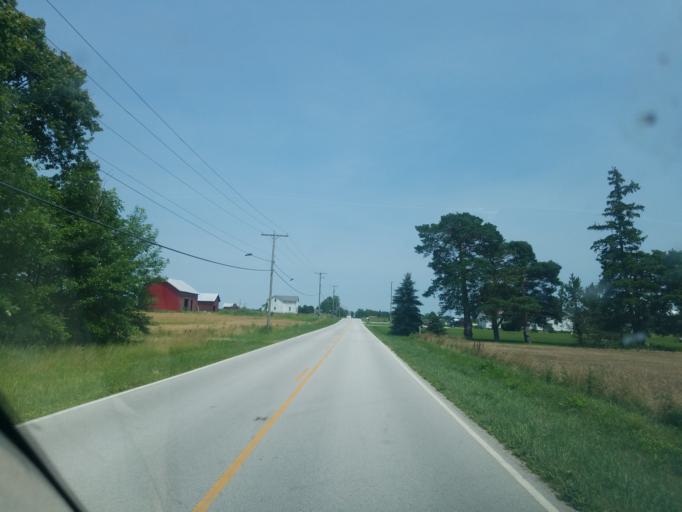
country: US
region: Ohio
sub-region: Wyandot County
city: Carey
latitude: 41.0506
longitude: -83.3316
